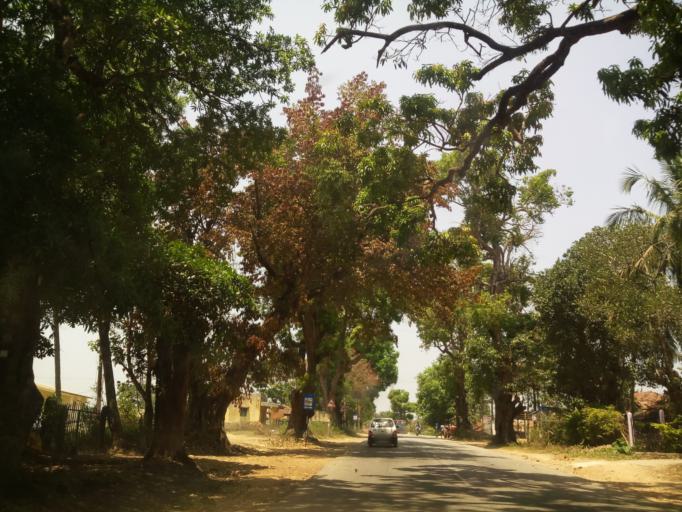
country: IN
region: Karnataka
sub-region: Hassan
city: Alur
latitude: 12.9493
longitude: 75.9434
